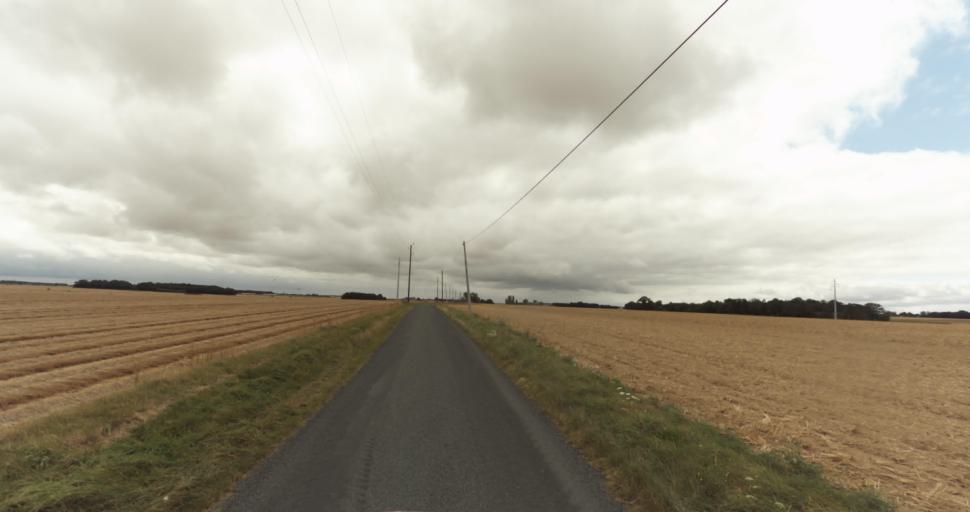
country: FR
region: Haute-Normandie
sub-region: Departement de l'Eure
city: Evreux
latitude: 48.9106
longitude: 1.2084
